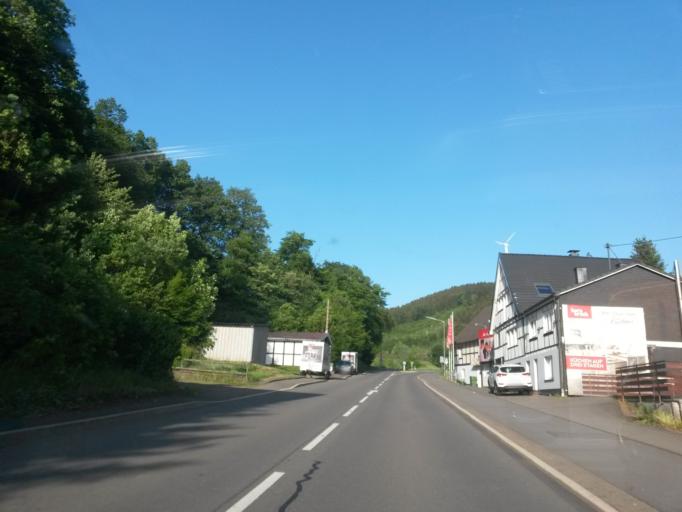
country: DE
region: North Rhine-Westphalia
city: Bergneustadt
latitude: 51.0411
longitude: 7.7127
